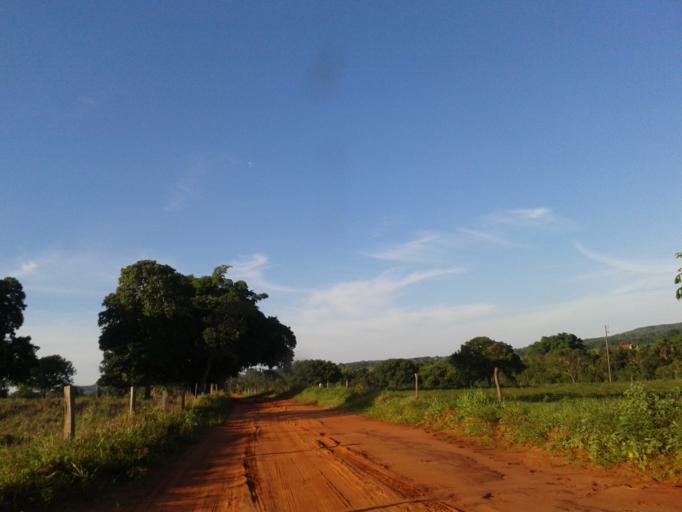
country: BR
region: Minas Gerais
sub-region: Santa Vitoria
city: Santa Vitoria
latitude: -18.9346
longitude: -49.8576
